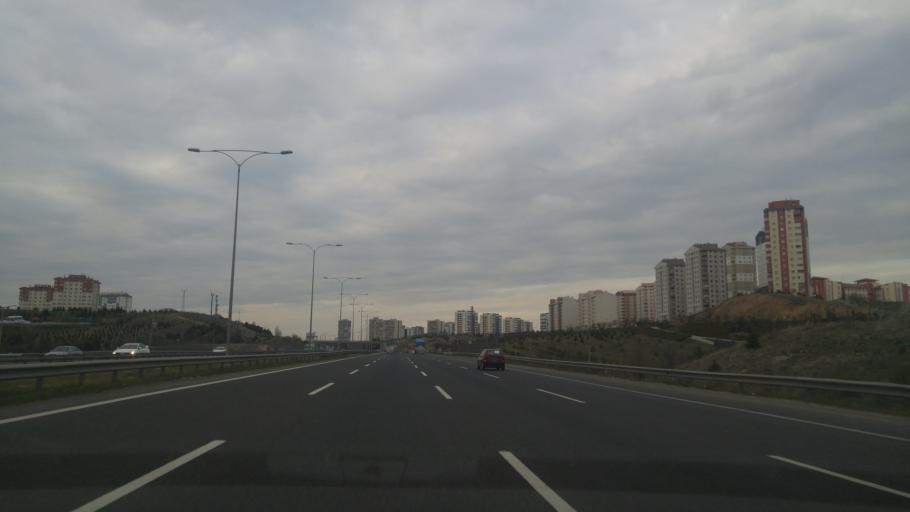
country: TR
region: Ankara
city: Etimesgut
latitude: 39.9907
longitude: 32.6370
